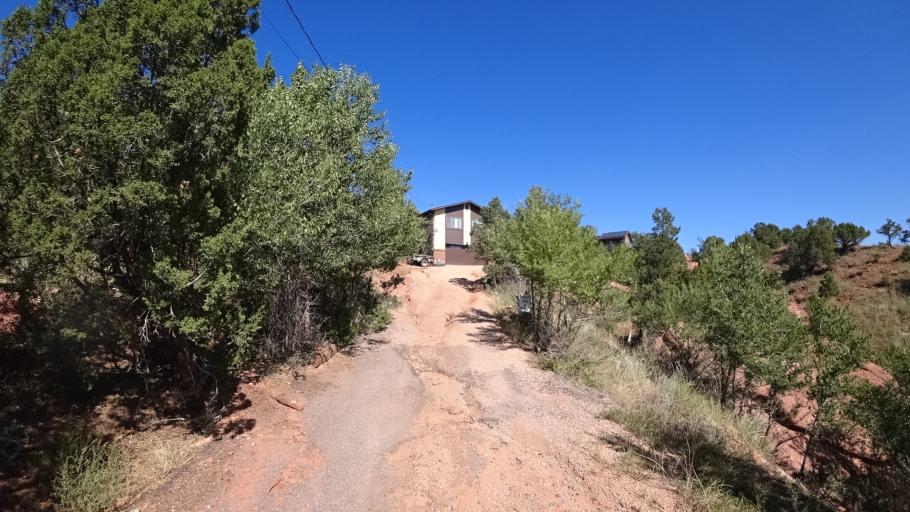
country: US
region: Colorado
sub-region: El Paso County
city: Manitou Springs
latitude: 38.8616
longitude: -104.8864
